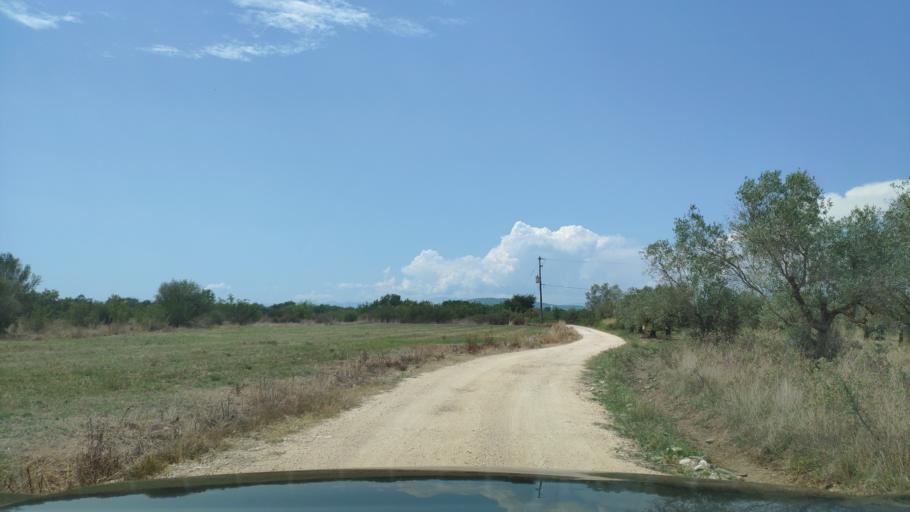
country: GR
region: West Greece
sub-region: Nomos Aitolias kai Akarnanias
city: Menidi
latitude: 39.0539
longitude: 21.0977
